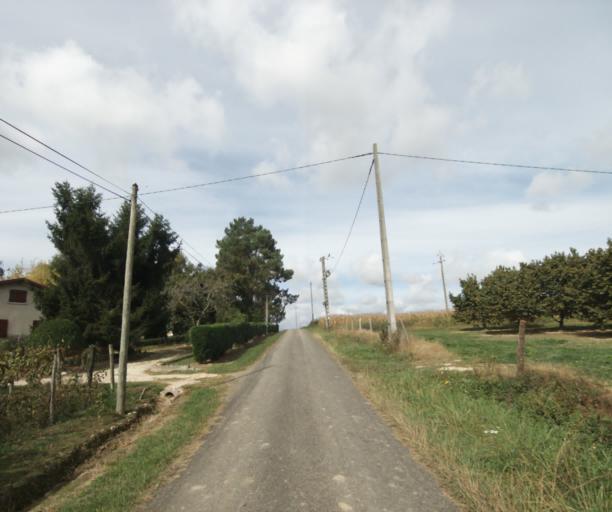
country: FR
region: Midi-Pyrenees
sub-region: Departement du Gers
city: Eauze
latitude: 43.8678
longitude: 0.0740
